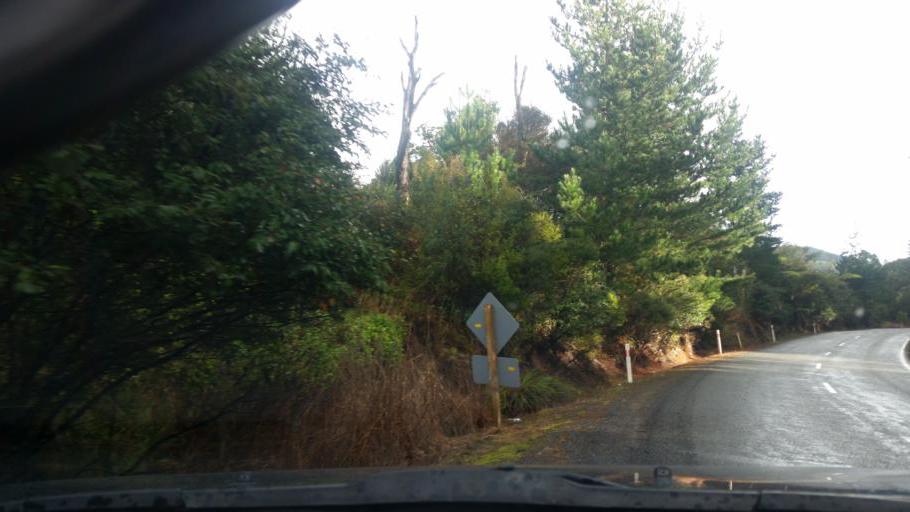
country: NZ
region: Northland
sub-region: Kaipara District
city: Dargaville
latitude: -35.7282
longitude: 173.8618
